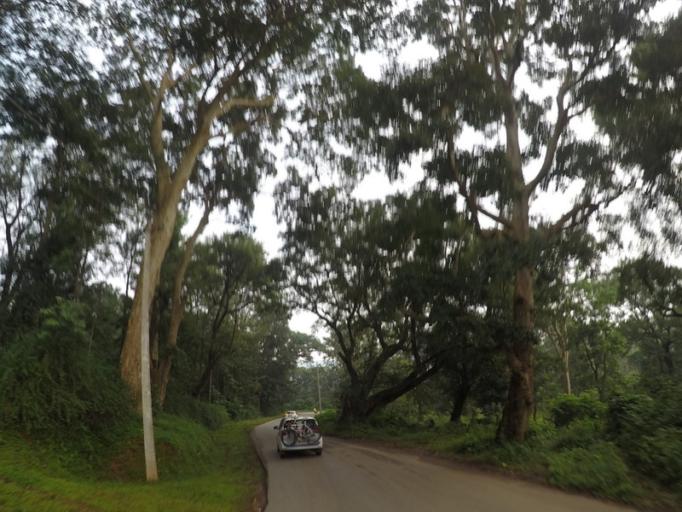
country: IN
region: Karnataka
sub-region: Chikmagalur
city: Chikmagalur
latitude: 13.4704
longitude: 75.7993
